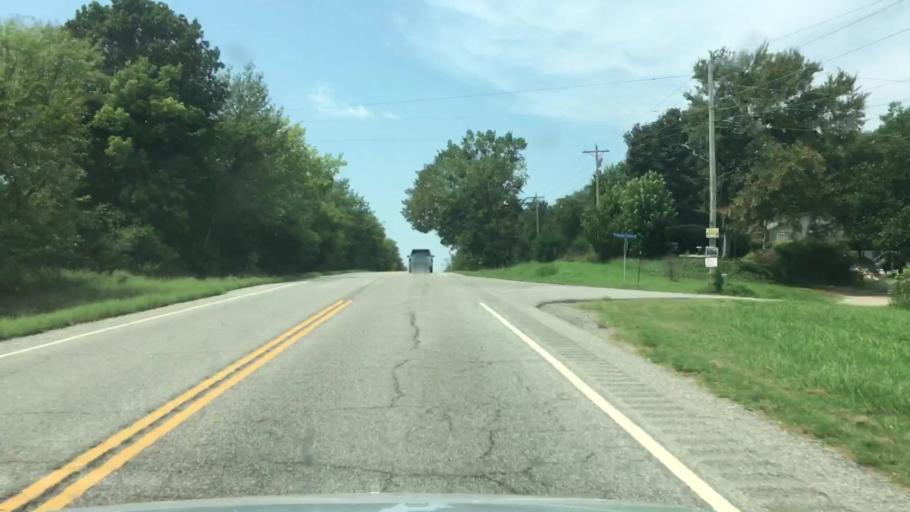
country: US
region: Oklahoma
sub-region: Wagoner County
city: Wagoner
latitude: 35.9297
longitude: -95.2431
